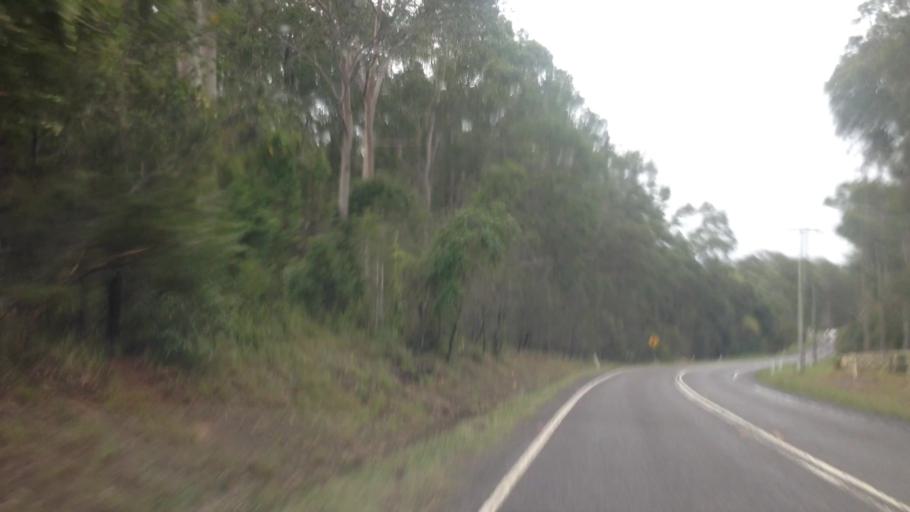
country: AU
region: New South Wales
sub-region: Wyong Shire
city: Little Jilliby
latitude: -33.2606
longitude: 151.3983
